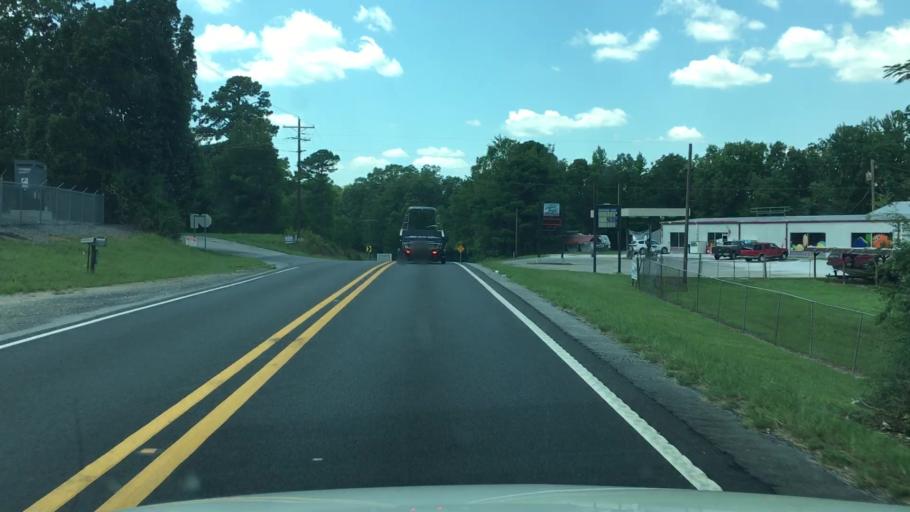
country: US
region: Arkansas
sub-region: Clark County
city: Arkadelphia
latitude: 34.2558
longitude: -93.1281
